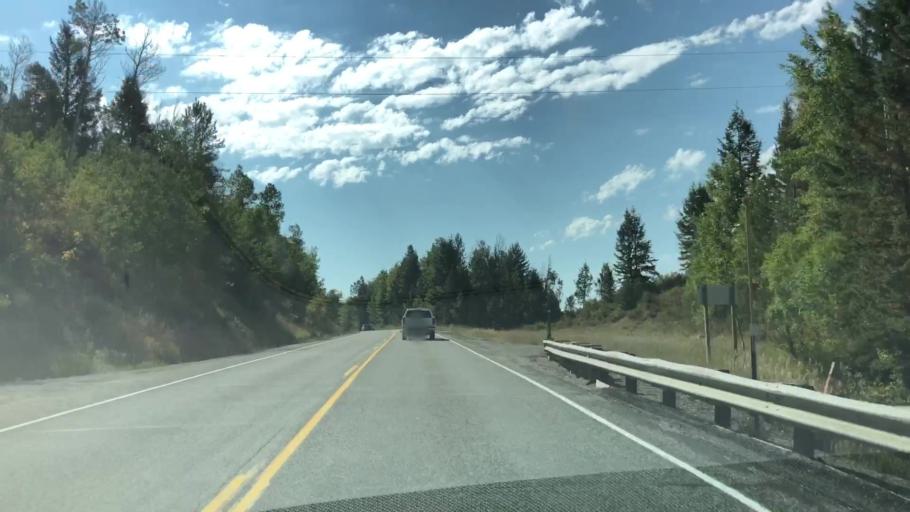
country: US
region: Idaho
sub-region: Teton County
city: Victor
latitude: 43.2824
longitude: -111.1191
